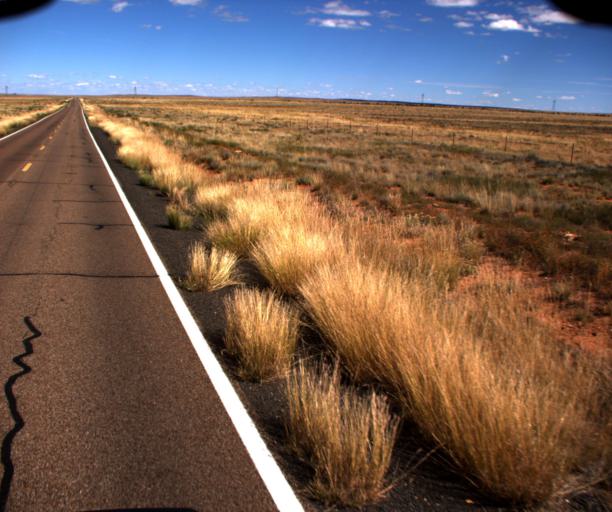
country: US
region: Arizona
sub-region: Navajo County
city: Holbrook
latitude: 34.7788
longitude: -110.2344
